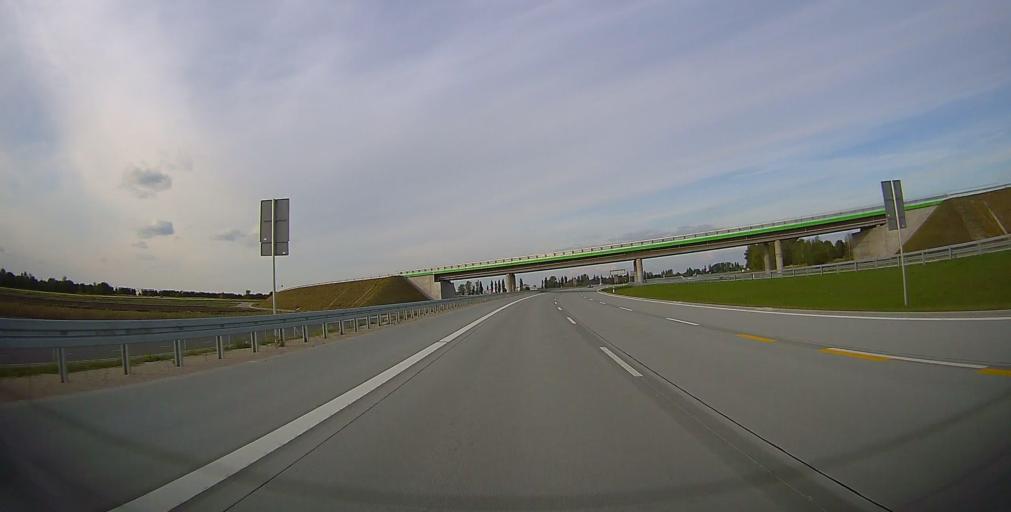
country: PL
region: Masovian Voivodeship
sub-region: Powiat piaseczynski
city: Lesznowola
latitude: 52.1010
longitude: 20.9700
